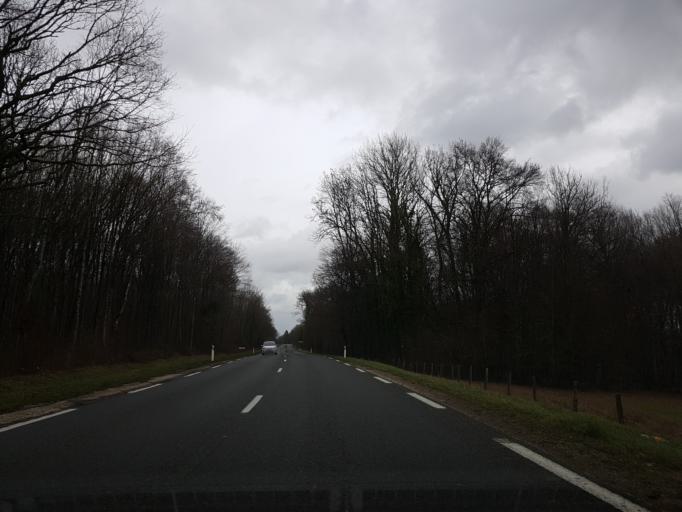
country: FR
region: Champagne-Ardenne
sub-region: Departement de la Haute-Marne
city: Fayl-Billot
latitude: 47.8099
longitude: 5.5318
